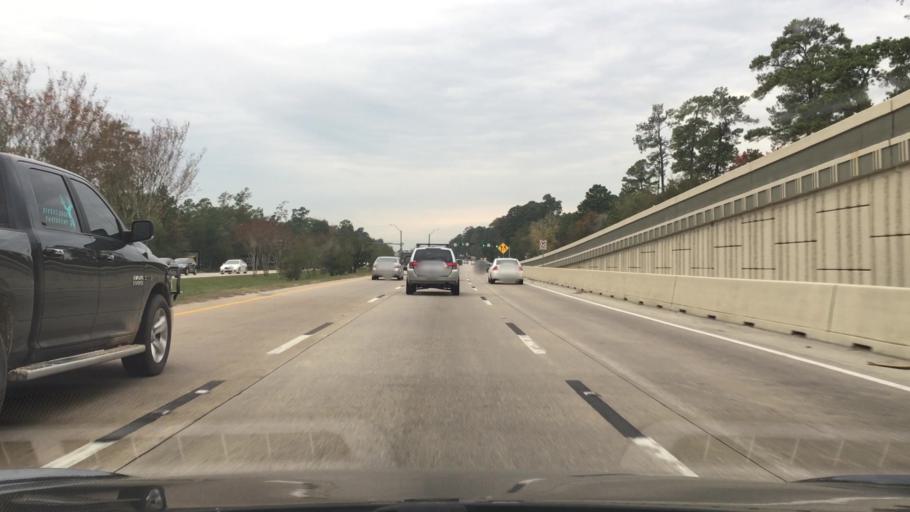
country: US
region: Texas
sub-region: Montgomery County
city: Shenandoah
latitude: 30.2073
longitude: -95.4614
